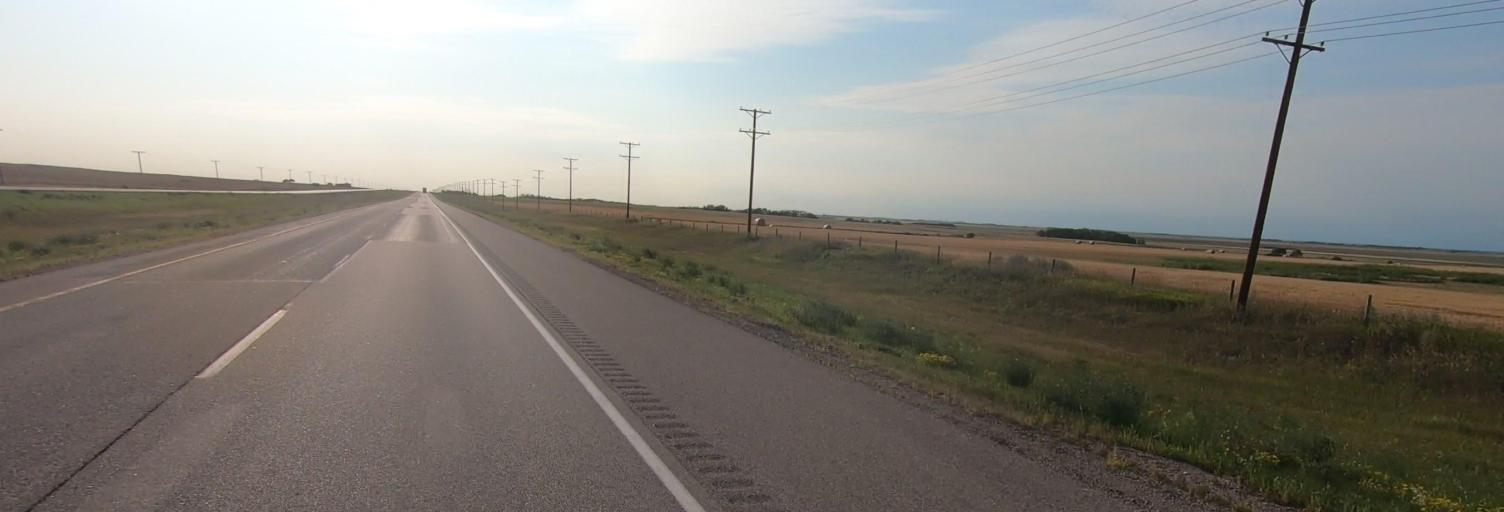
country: CA
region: Saskatchewan
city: Melville
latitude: 50.4116
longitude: -102.9931
